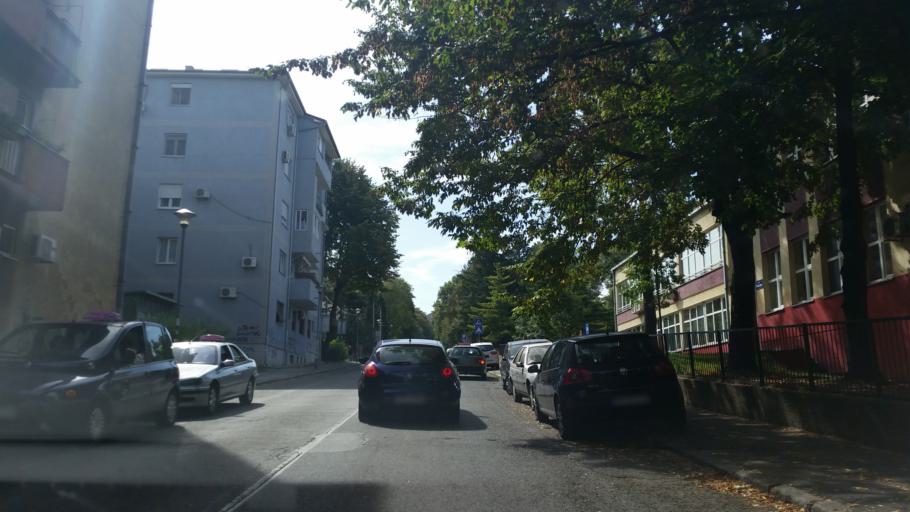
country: RS
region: Central Serbia
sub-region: Belgrade
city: Palilula
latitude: 44.8128
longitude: 20.5169
